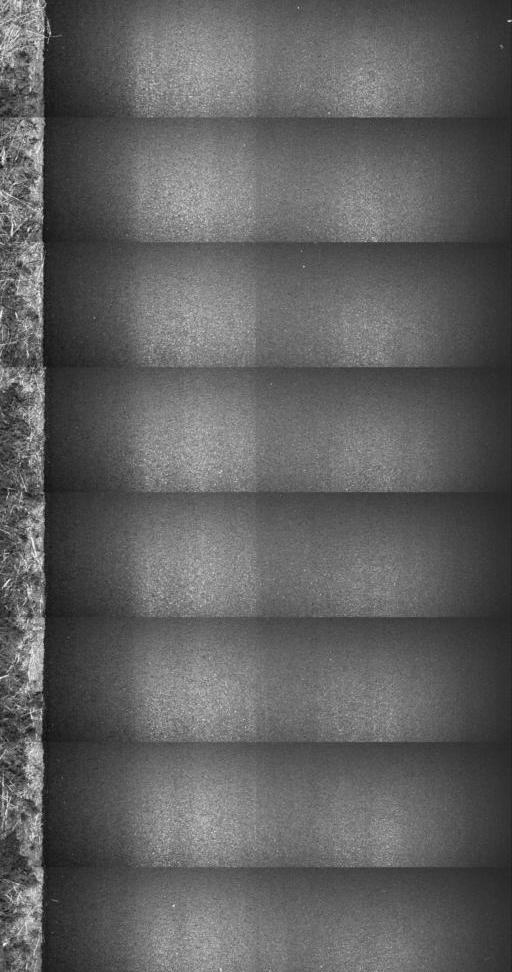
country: US
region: Vermont
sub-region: Orange County
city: Chelsea
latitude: 43.9670
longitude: -72.5547
